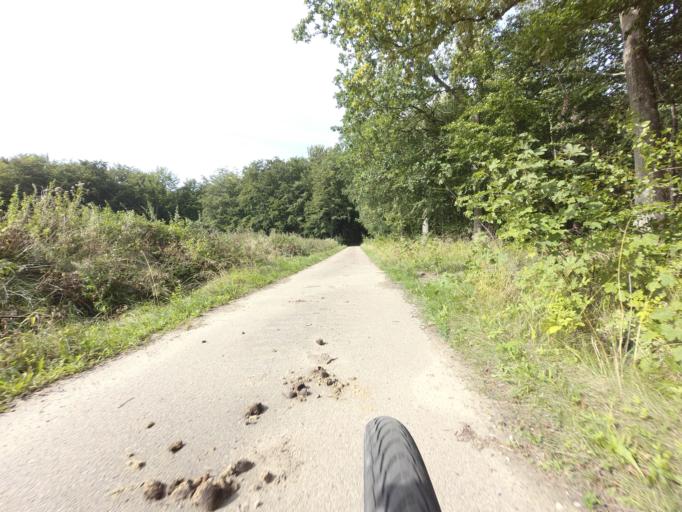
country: DK
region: Zealand
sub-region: Faxe Kommune
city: Fakse Ladeplads
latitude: 55.2349
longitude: 12.1903
